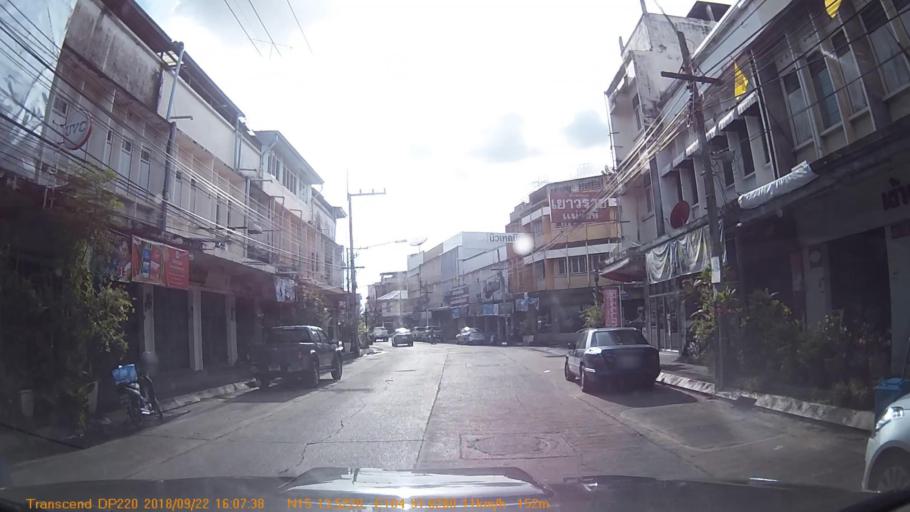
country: TH
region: Changwat Ubon Ratchathani
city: Ubon Ratchathani
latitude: 15.2254
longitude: 104.8603
